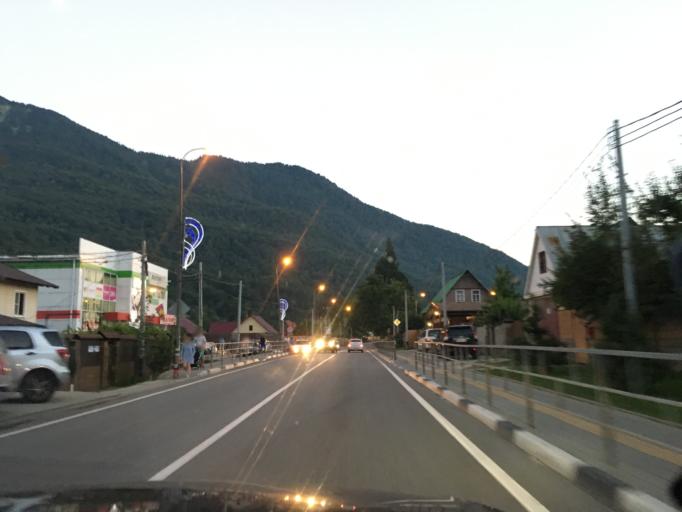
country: RU
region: Krasnodarskiy
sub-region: Sochi City
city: Krasnaya Polyana
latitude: 43.6816
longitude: 40.2126
